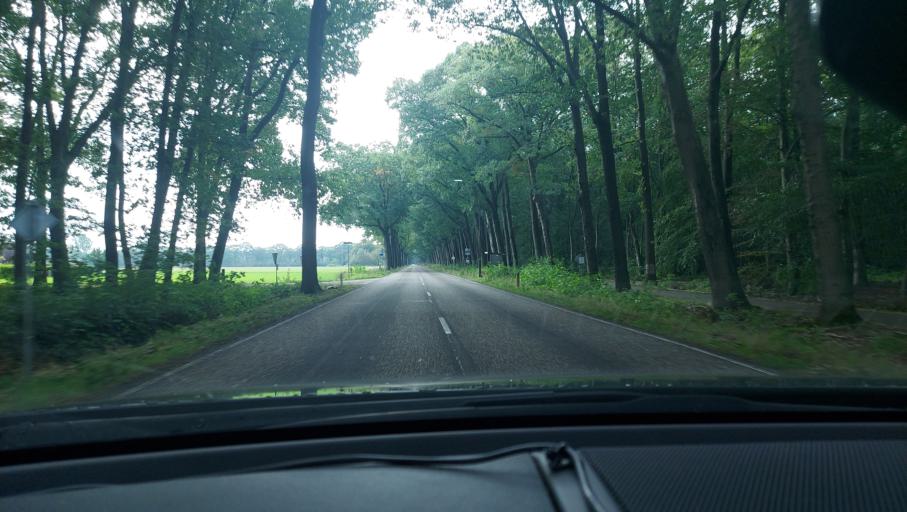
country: NL
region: North Brabant
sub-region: Gemeente Sint Anthonis
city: Sint Anthonis
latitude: 51.5452
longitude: 5.8043
